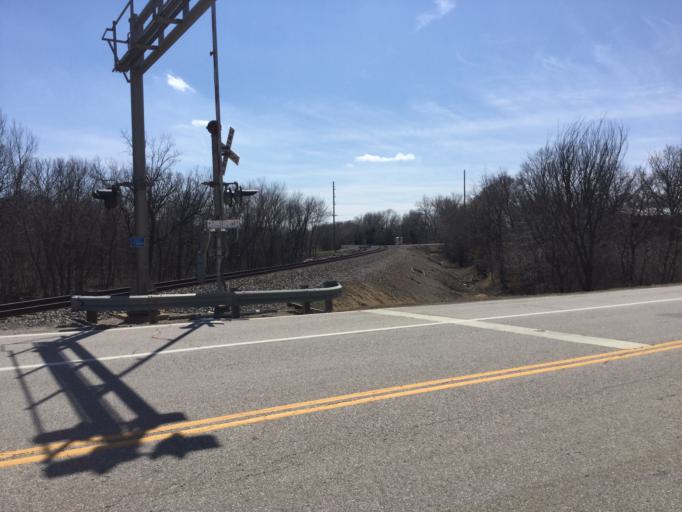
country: US
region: Kansas
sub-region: Wilson County
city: Fredonia
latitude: 37.6313
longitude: -95.7472
